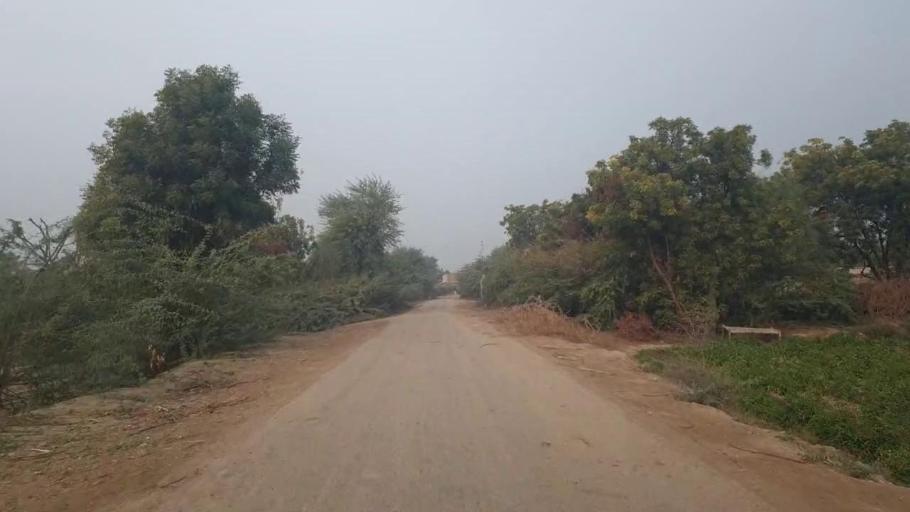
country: PK
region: Sindh
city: Tando Adam
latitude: 25.7102
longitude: 68.6485
